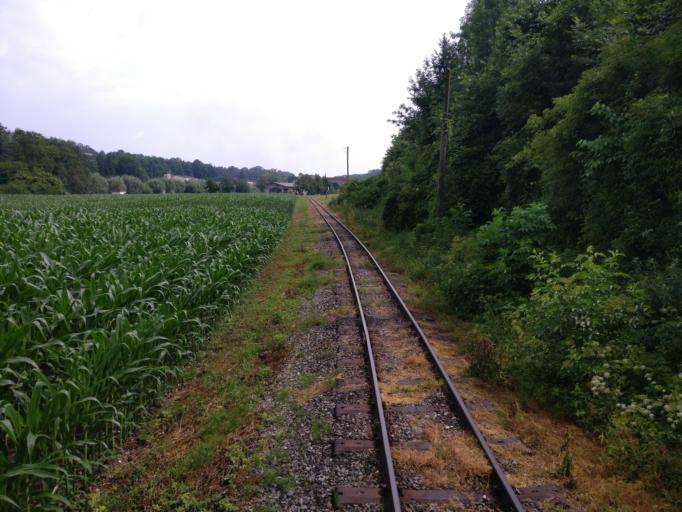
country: AT
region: Upper Austria
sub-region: Politischer Bezirk Steyr-Land
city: Sierning
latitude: 48.0043
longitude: 14.2989
